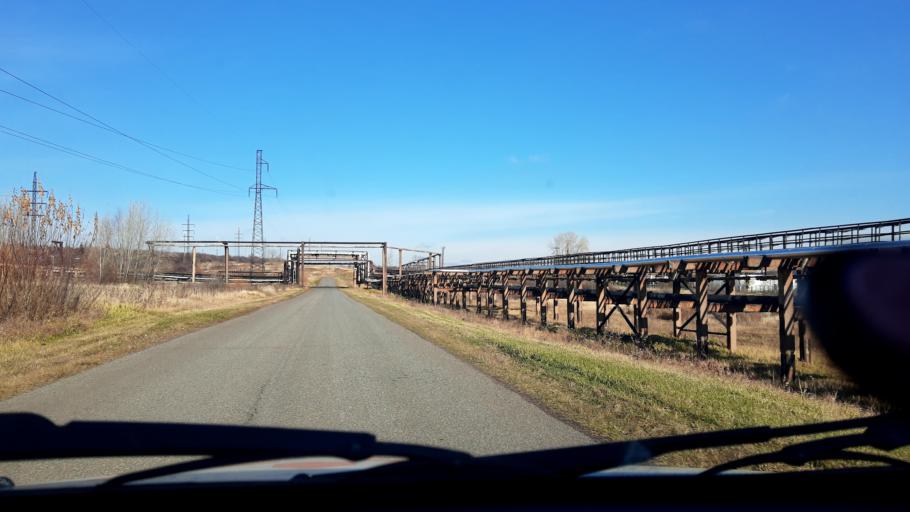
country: RU
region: Bashkortostan
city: Blagoveshchensk
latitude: 54.8861
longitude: 56.1021
